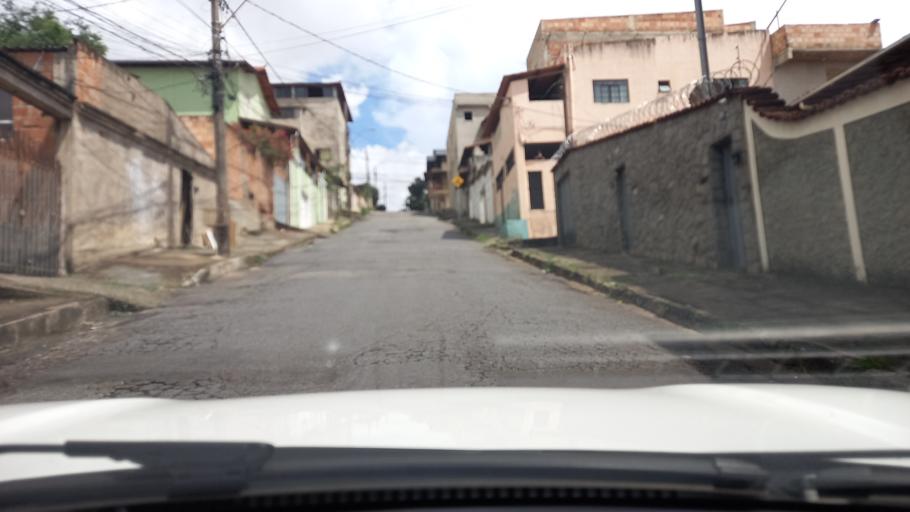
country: BR
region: Minas Gerais
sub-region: Contagem
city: Contagem
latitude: -19.9056
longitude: -44.0250
